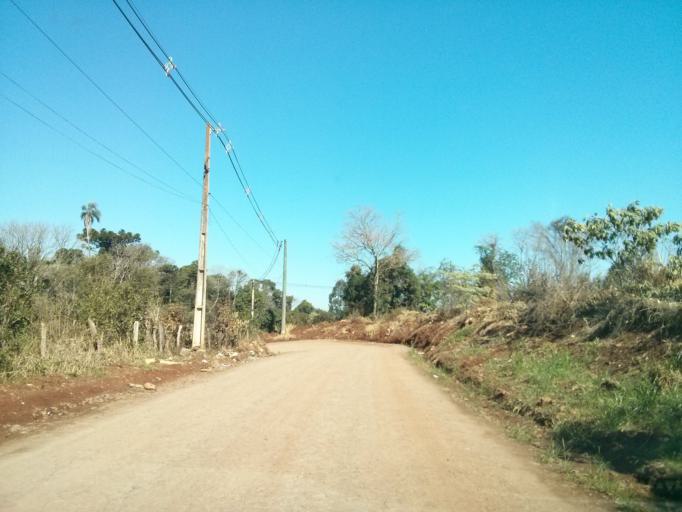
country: BR
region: Santa Catarina
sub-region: Chapeco
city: Chapeco
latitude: -27.0944
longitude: -52.6943
